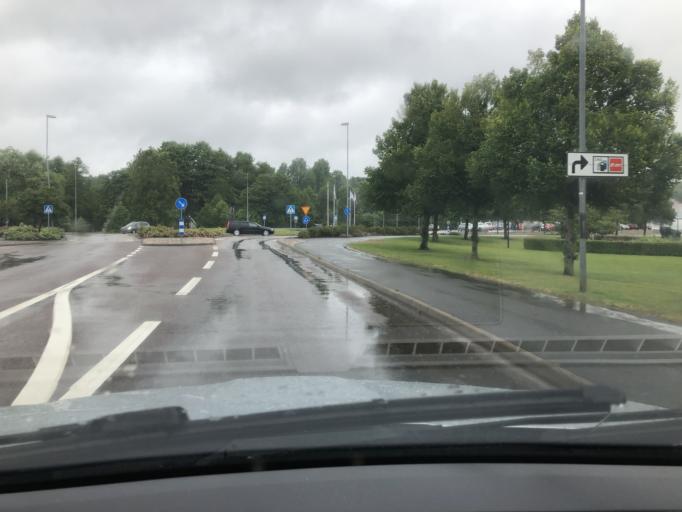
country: SE
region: Blekinge
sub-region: Olofstroms Kommun
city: Olofstroem
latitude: 56.2765
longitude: 14.5342
